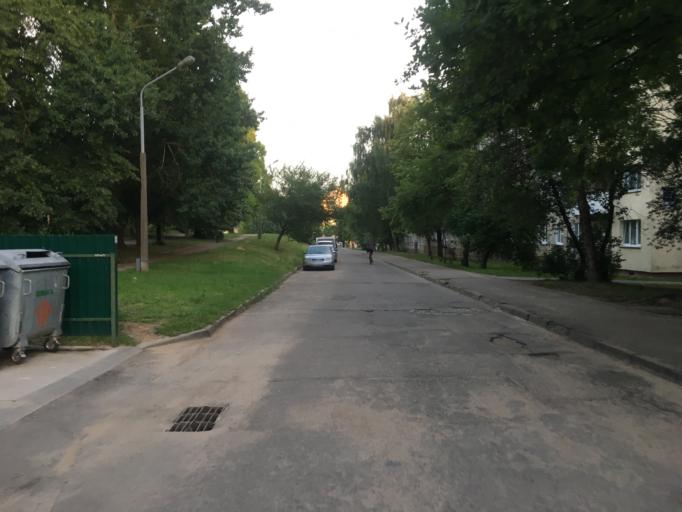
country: BY
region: Grodnenskaya
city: Hrodna
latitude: 53.6994
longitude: 23.8035
